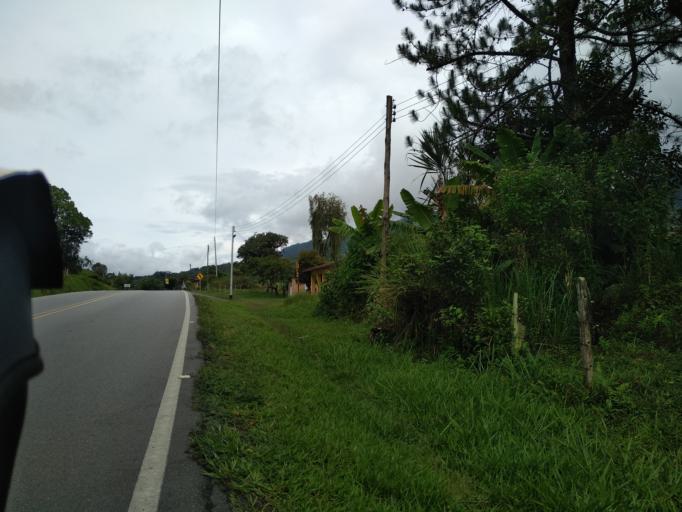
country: CO
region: Santander
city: Suaita
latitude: 6.0970
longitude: -73.3814
